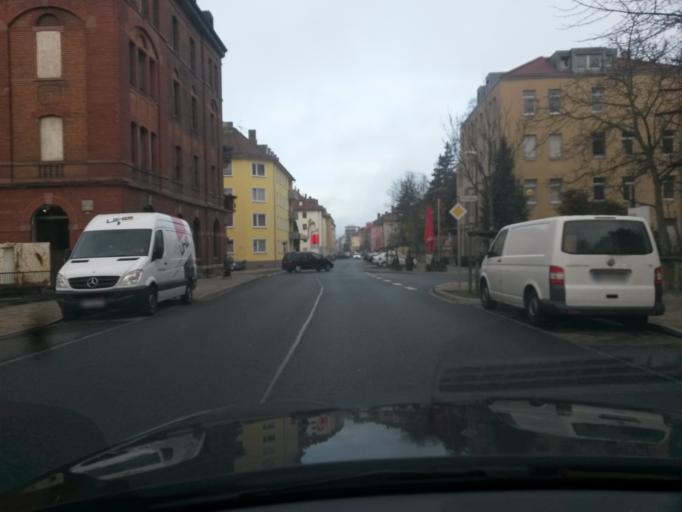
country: DE
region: Bavaria
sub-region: Regierungsbezirk Unterfranken
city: Wuerzburg
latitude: 49.7780
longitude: 9.9387
